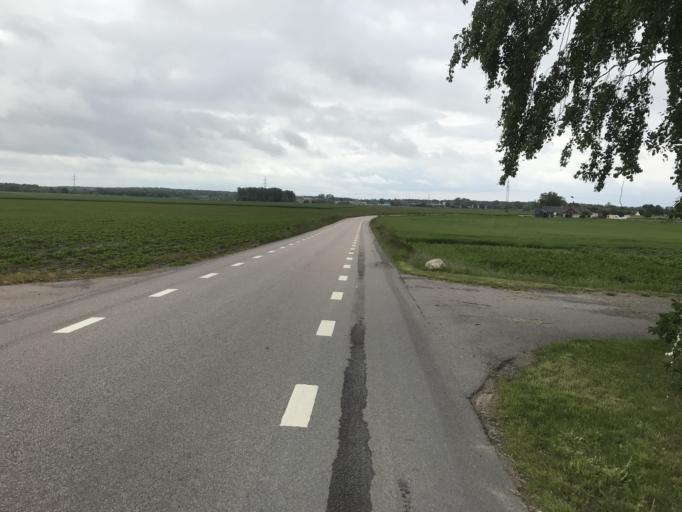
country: SE
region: Skane
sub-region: Landskrona
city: Asmundtorp
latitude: 55.8670
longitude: 12.9261
